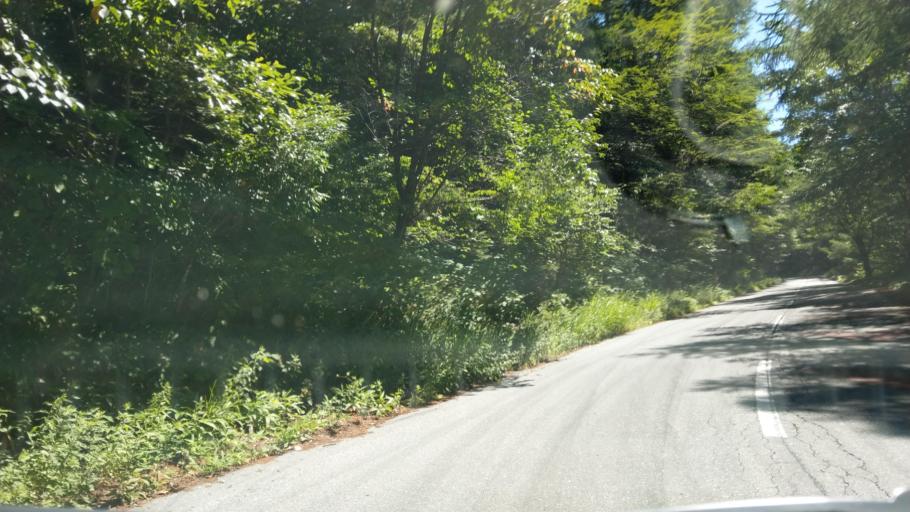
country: JP
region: Nagano
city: Komoro
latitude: 36.3894
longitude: 138.4656
